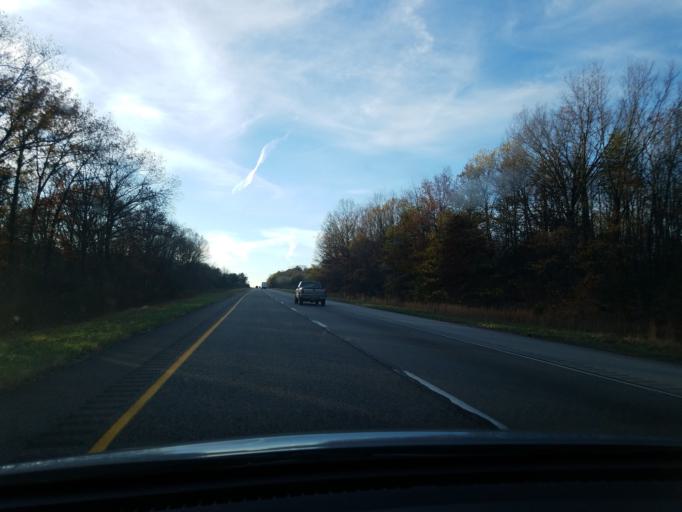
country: US
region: Indiana
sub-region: Warrick County
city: Boonville
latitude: 38.1993
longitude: -87.1783
